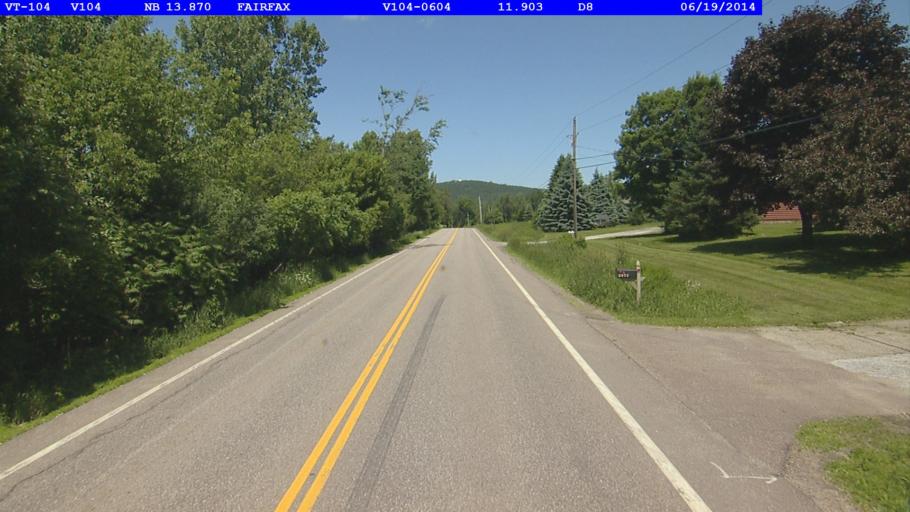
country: US
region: Vermont
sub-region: Franklin County
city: Saint Albans
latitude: 44.7552
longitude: -73.0557
